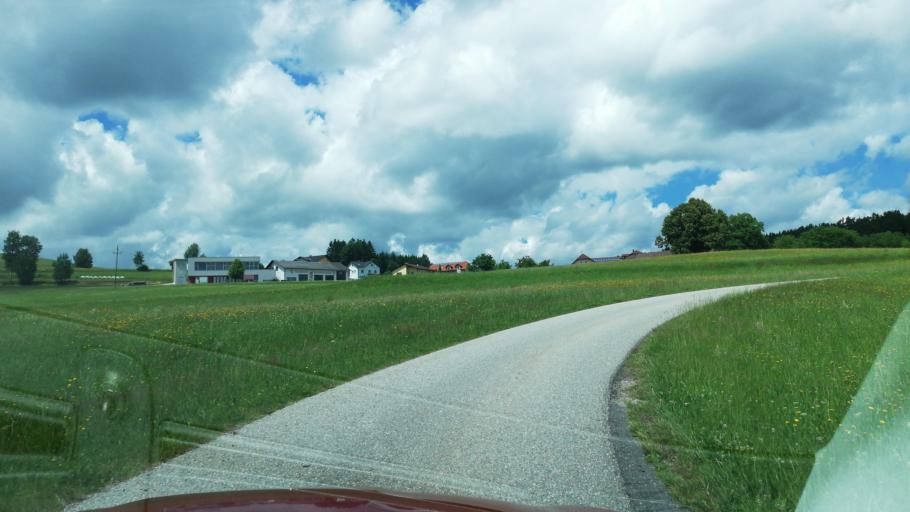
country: AT
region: Upper Austria
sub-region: Politischer Bezirk Urfahr-Umgebung
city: Haibach im Muhlkreis
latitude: 48.4252
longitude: 14.3602
